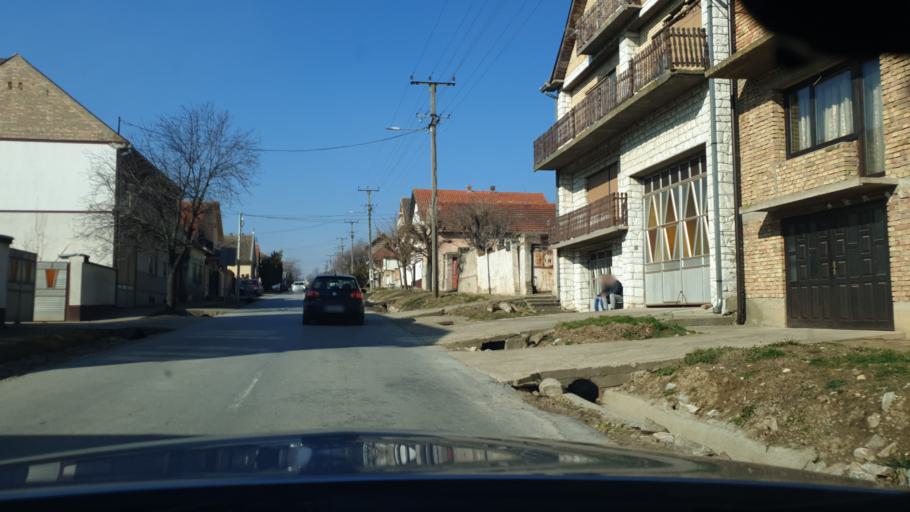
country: RS
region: Autonomna Pokrajina Vojvodina
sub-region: Sremski Okrug
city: Irig
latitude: 45.0895
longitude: 19.8344
